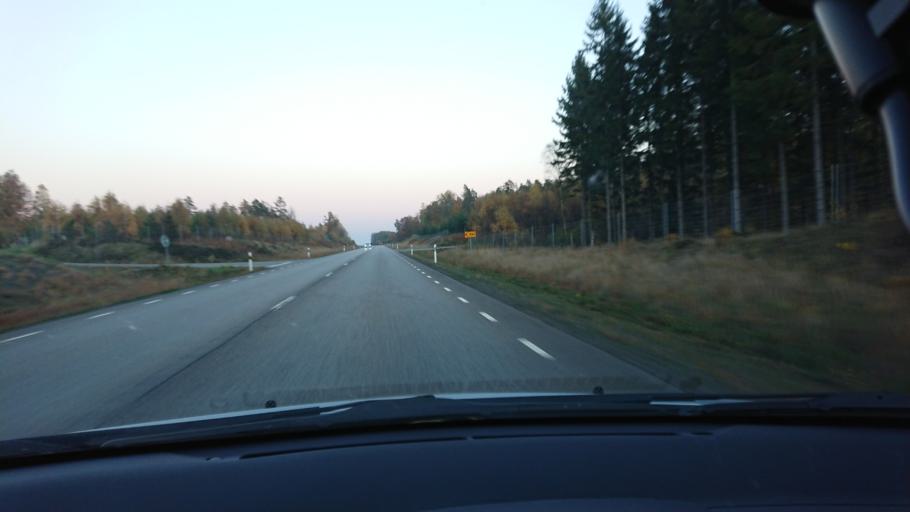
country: SE
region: Kronoberg
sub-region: Markaryds Kommun
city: Stromsnasbruk
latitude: 56.7518
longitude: 13.5193
